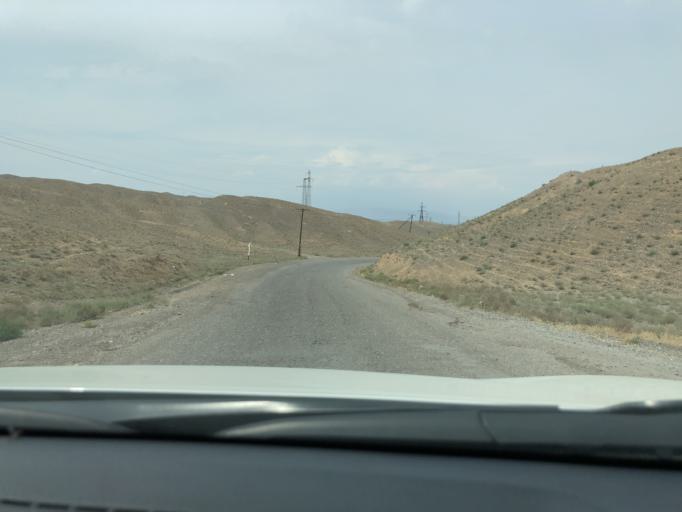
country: TJ
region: Viloyati Sughd
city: Kim
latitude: 40.2187
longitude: 70.4797
